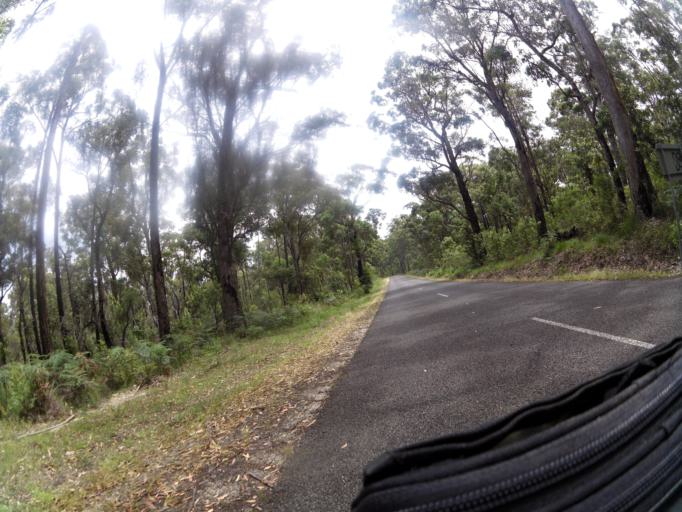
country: AU
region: Victoria
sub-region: East Gippsland
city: Lakes Entrance
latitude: -37.6971
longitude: 148.7412
